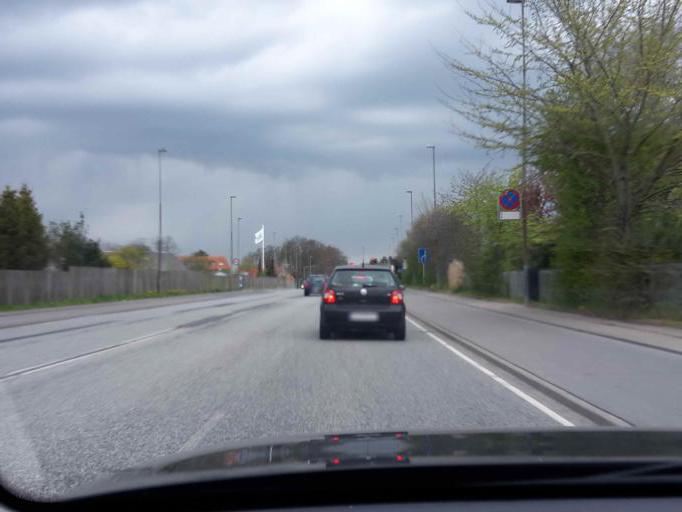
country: DK
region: South Denmark
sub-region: Odense Kommune
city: Odense
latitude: 55.4109
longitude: 10.3305
